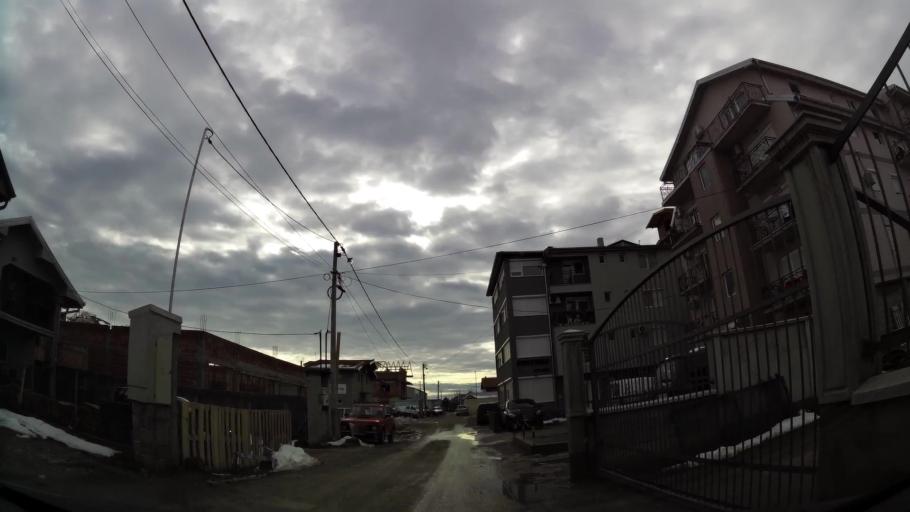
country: RS
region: Central Serbia
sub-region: Belgrade
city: Surcin
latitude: 44.8010
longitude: 20.3428
